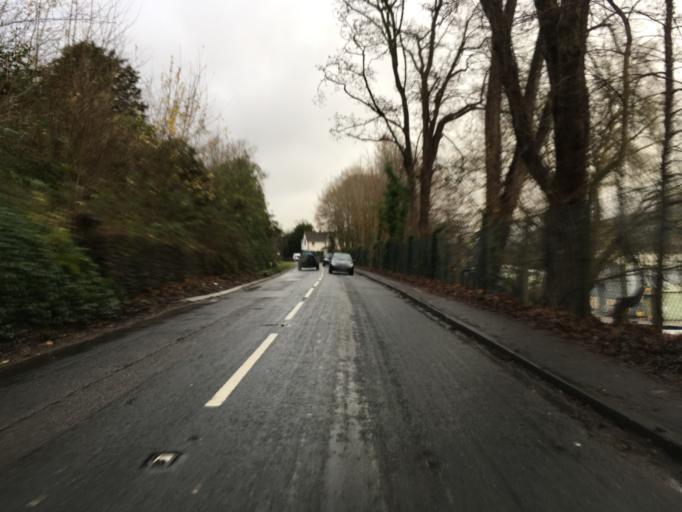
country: GB
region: England
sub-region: Gloucestershire
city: Nailsworth
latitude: 51.6943
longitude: -2.2148
